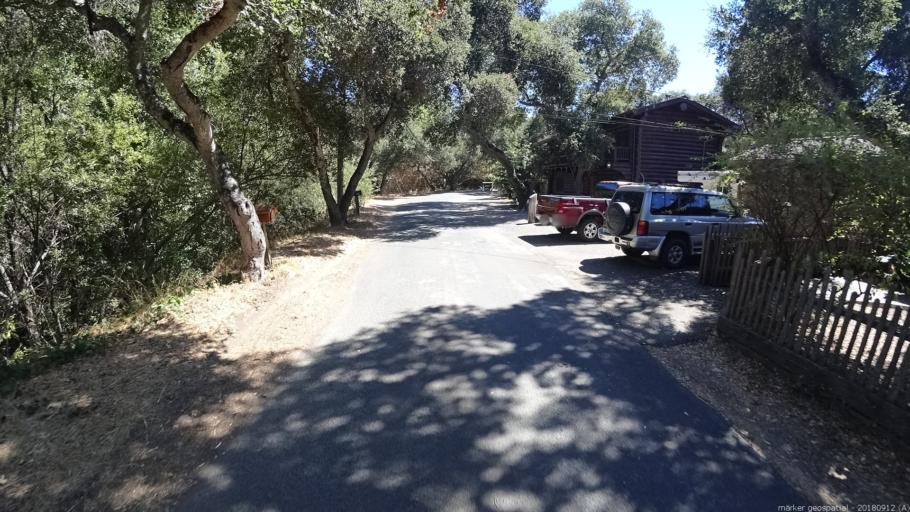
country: US
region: California
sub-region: Monterey County
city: Carmel Valley Village
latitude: 36.4739
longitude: -121.7266
